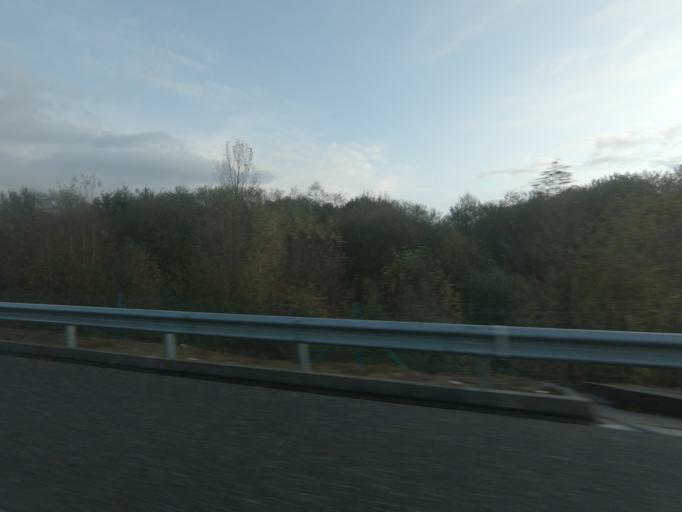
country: ES
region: Galicia
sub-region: Provincia de Pontevedra
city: Tui
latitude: 42.0902
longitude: -8.6418
